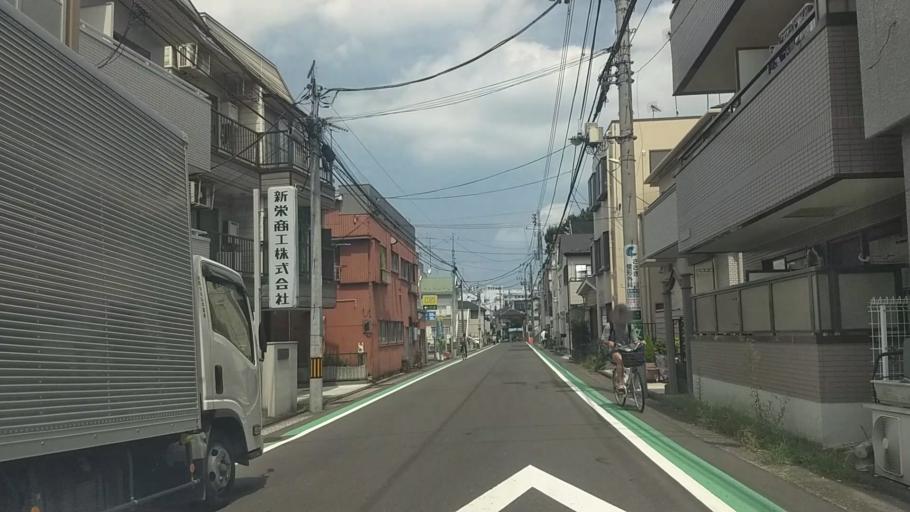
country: JP
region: Kanagawa
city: Yokohama
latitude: 35.5053
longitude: 139.6350
